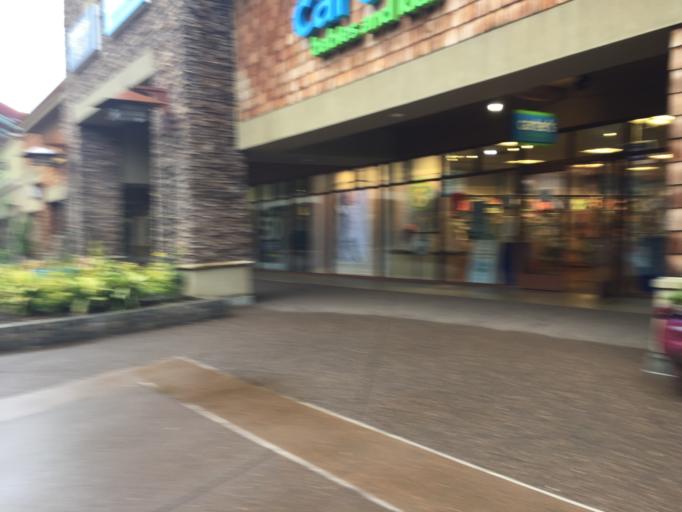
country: US
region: Oregon
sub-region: Marion County
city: Woodburn
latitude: 45.1558
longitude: -122.8795
